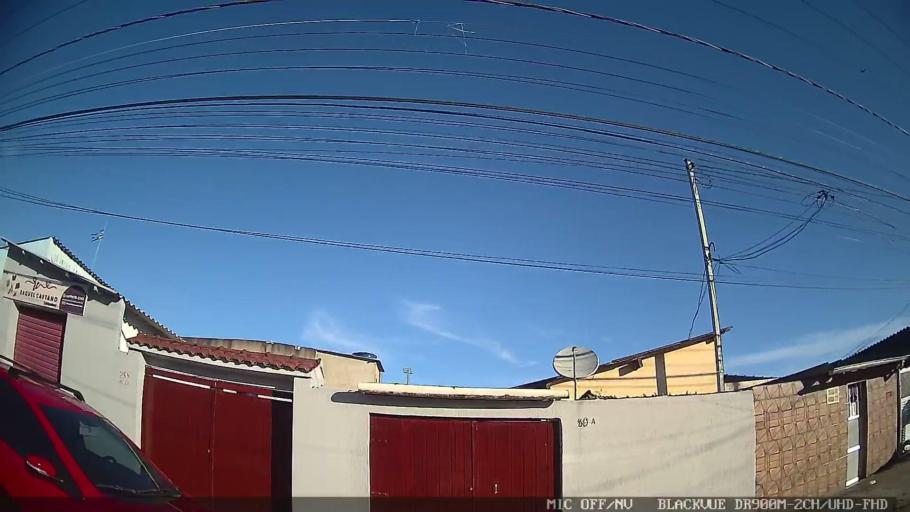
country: BR
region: Sao Paulo
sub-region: Santos
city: Santos
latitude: -23.9534
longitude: -46.2952
